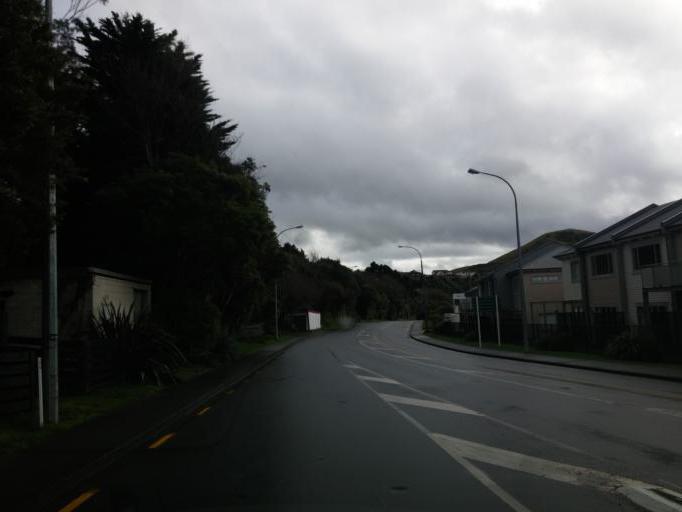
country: NZ
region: Wellington
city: Petone
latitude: -41.2076
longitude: 174.8119
